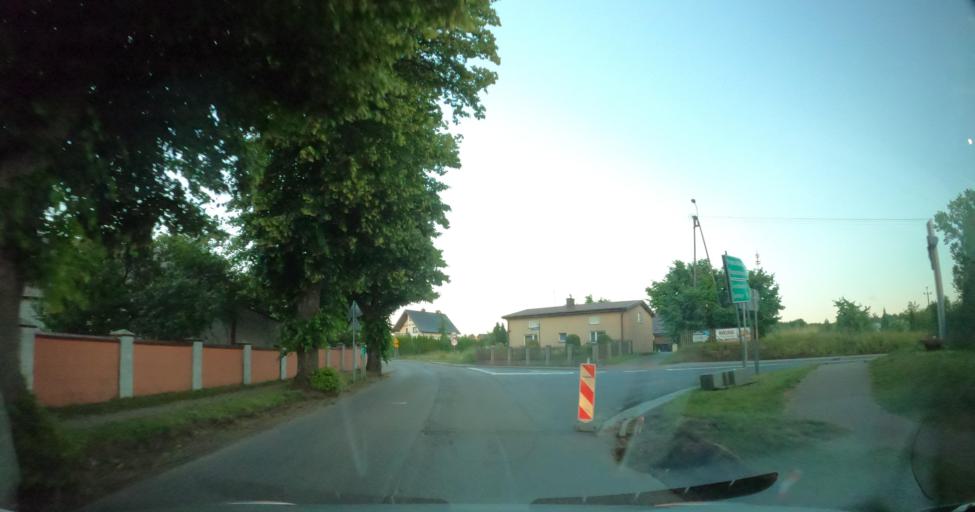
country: PL
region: Pomeranian Voivodeship
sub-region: Powiat wejherowski
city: Linia
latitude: 54.4515
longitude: 17.9278
